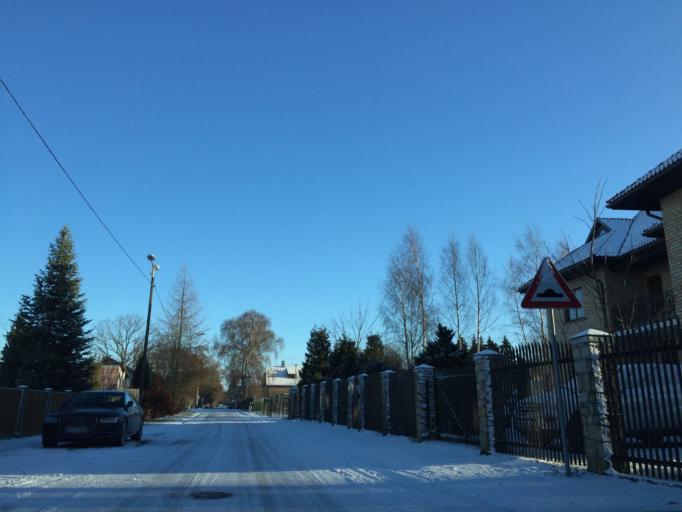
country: LV
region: Marupe
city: Marupe
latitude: 56.9110
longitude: 24.0602
